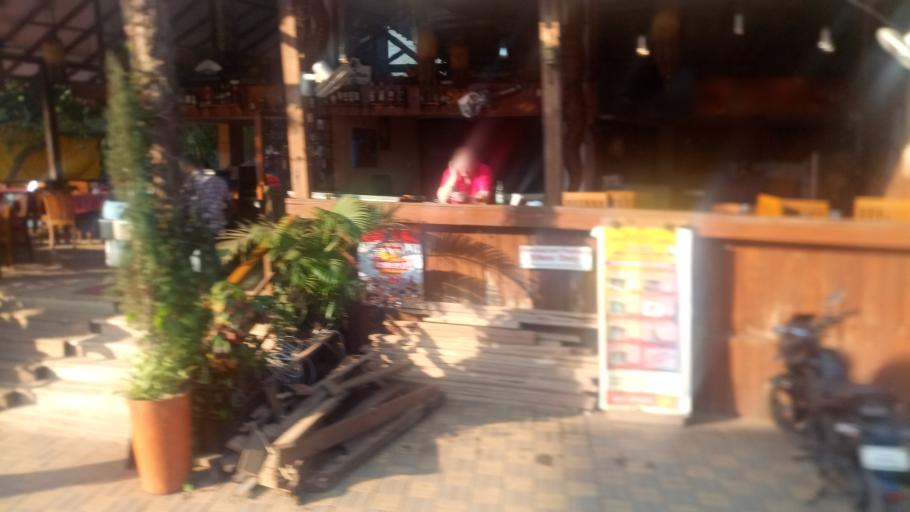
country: IN
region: Goa
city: Calangute
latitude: 15.5528
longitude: 73.7584
